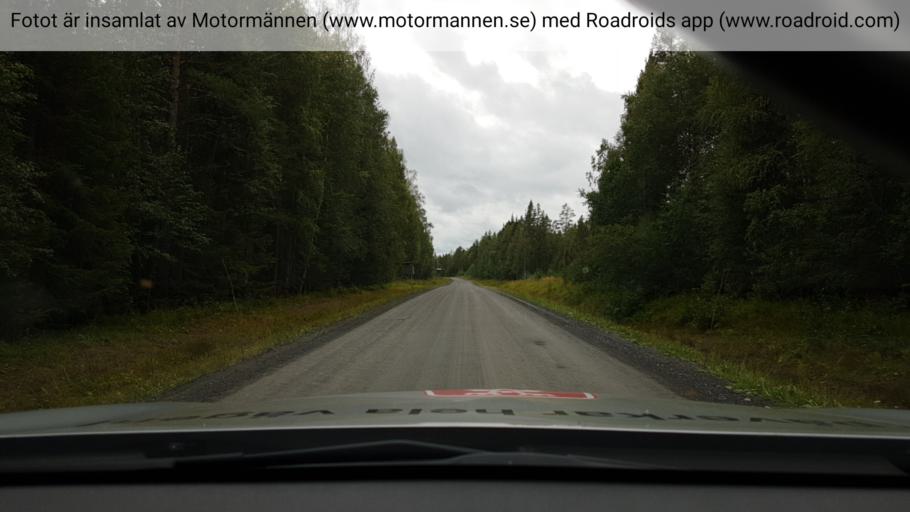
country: SE
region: Vaesterbotten
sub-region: Skelleftea Kommun
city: Forsbacka
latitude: 64.8300
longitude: 20.5004
